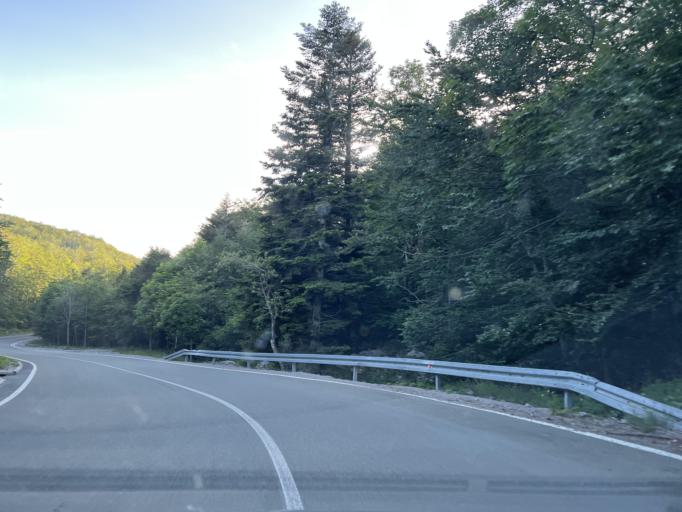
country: HR
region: Primorsko-Goranska
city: Podhum
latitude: 45.4142
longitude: 14.5601
